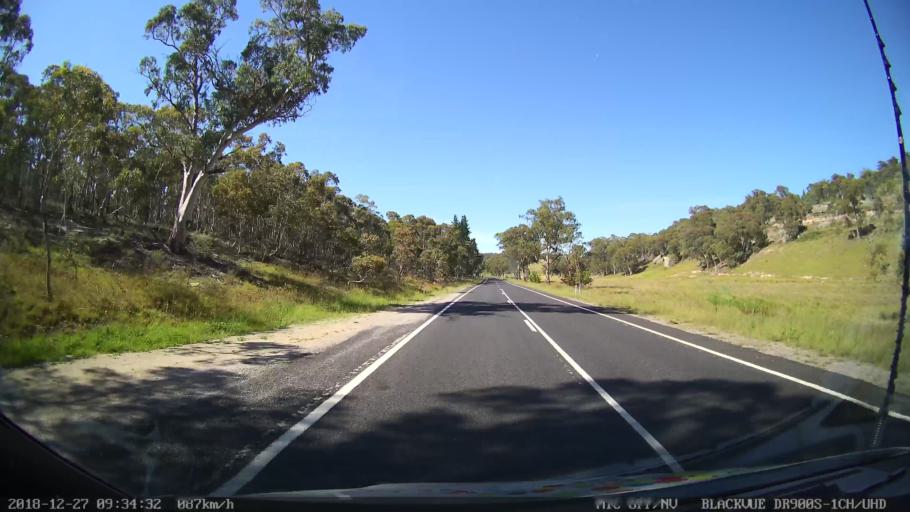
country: AU
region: New South Wales
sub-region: Lithgow
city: Portland
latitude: -33.2274
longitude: 150.0275
